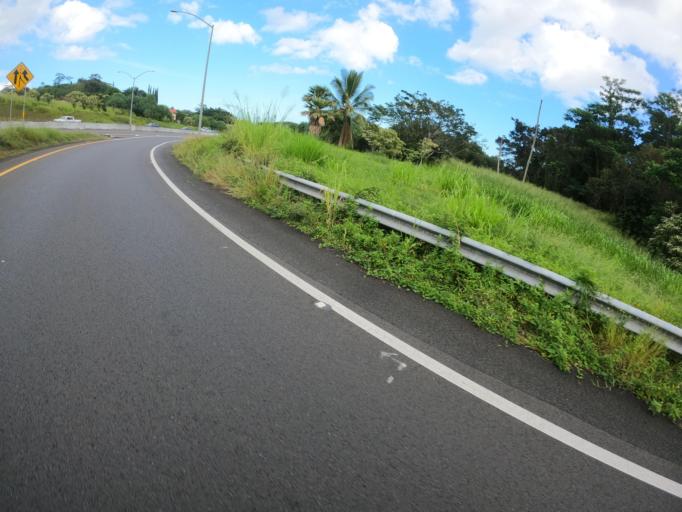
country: US
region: Hawaii
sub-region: Honolulu County
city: Kane'ohe
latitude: 21.4013
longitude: -157.8086
